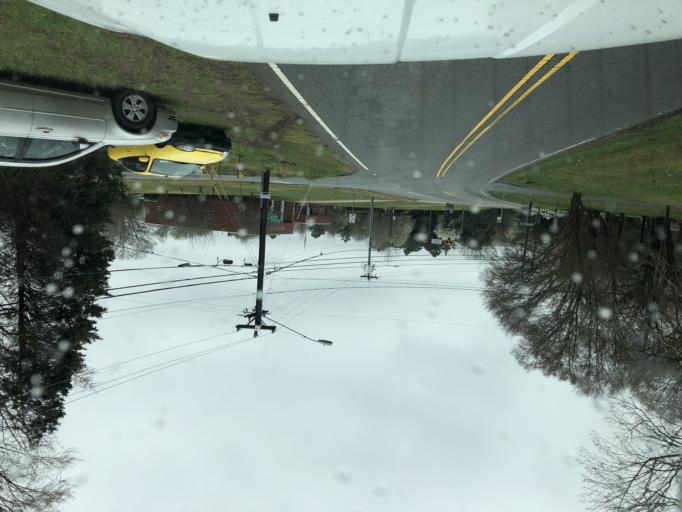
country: US
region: North Carolina
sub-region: Gaston County
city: Mount Holly
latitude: 35.3155
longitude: -80.9637
